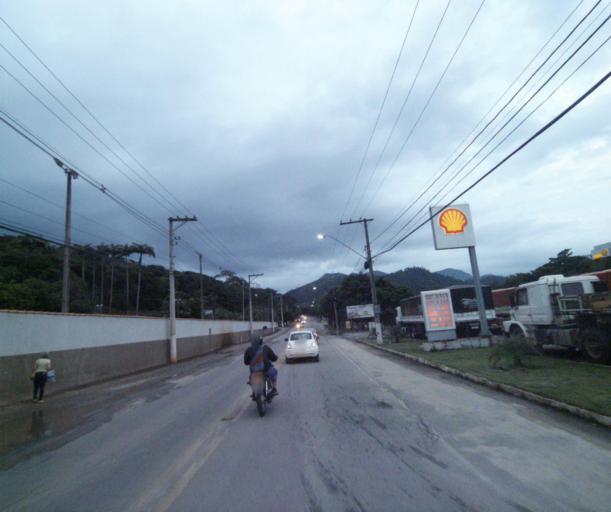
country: BR
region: Espirito Santo
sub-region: Castelo
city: Castelo
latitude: -20.6291
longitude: -41.2034
